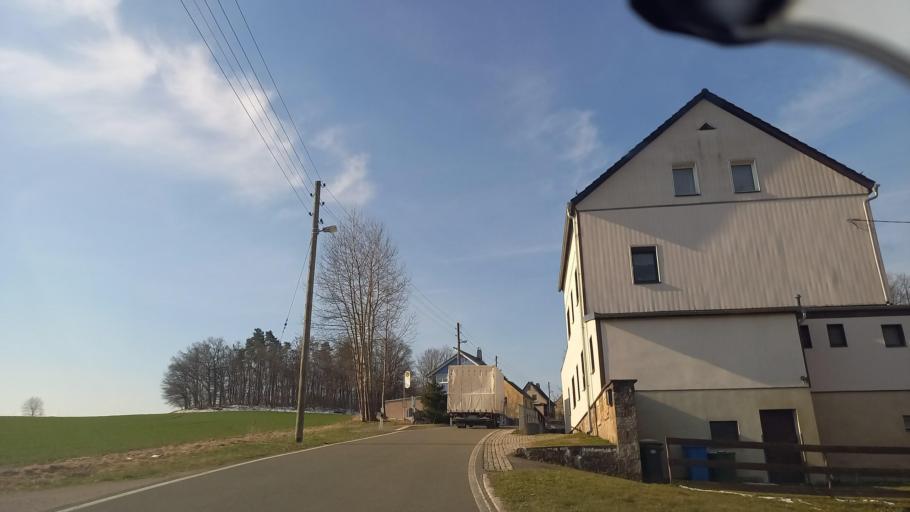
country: DE
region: Saxony
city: Kirchberg
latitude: 50.6014
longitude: 12.5238
